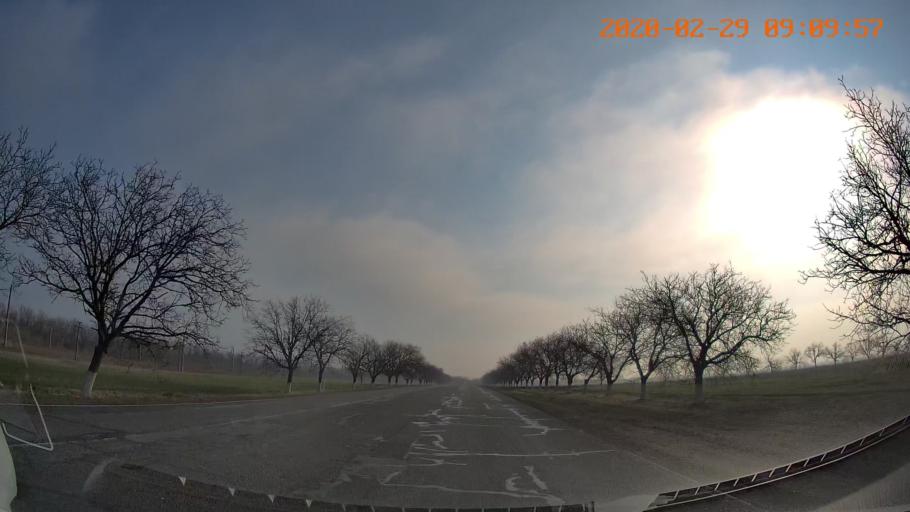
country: MD
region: Telenesti
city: Slobozia
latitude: 46.8449
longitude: 29.7724
